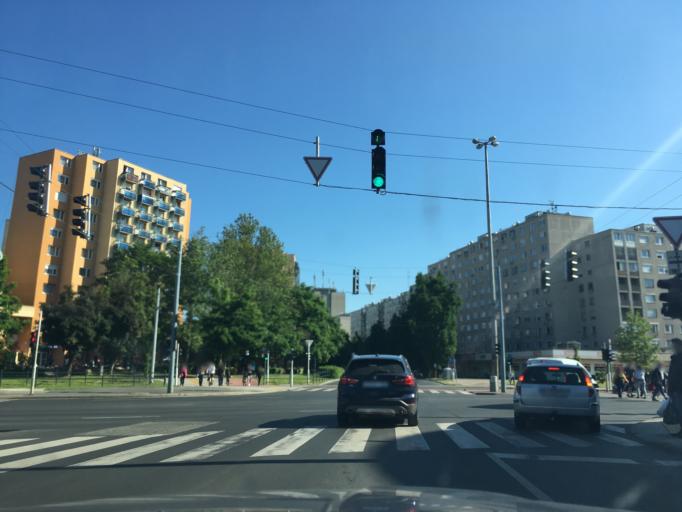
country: HU
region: Hajdu-Bihar
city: Debrecen
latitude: 47.5343
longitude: 21.6209
